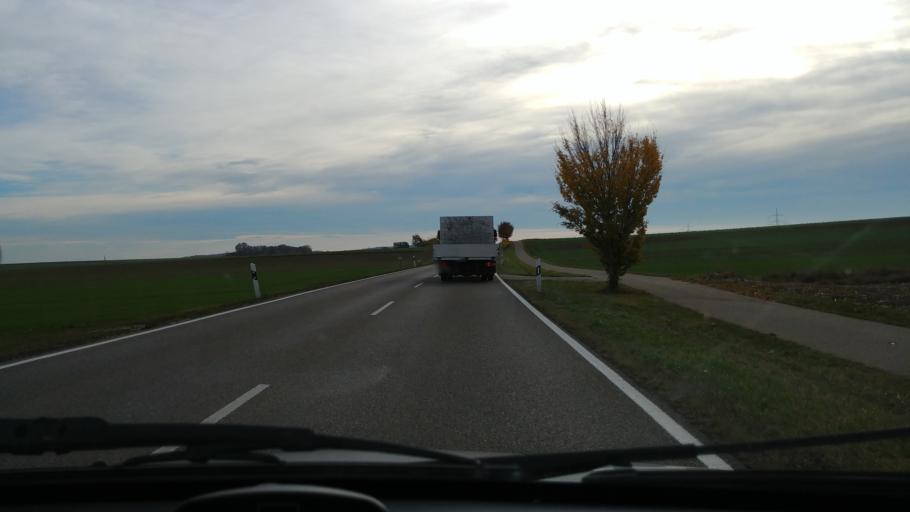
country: DE
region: Bavaria
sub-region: Swabia
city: Bachhagel
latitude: 48.6345
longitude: 10.2952
